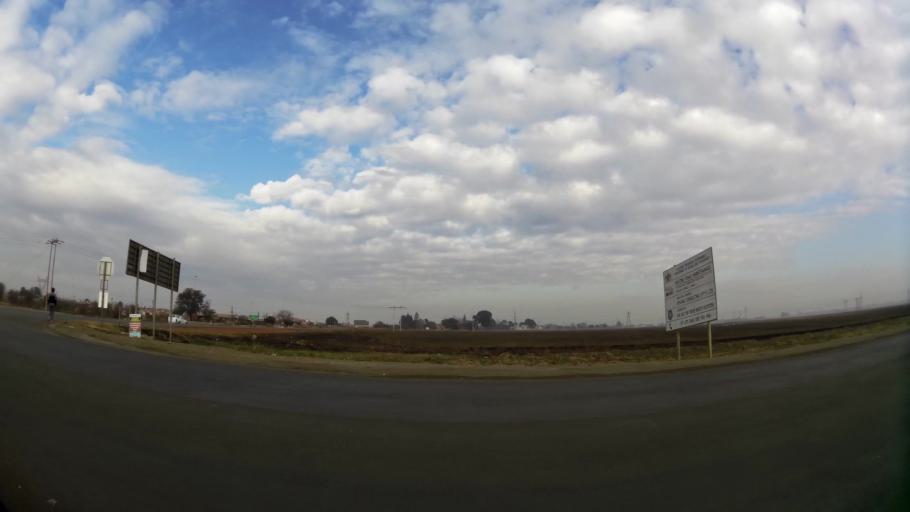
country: ZA
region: Gauteng
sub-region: Sedibeng District Municipality
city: Vanderbijlpark
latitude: -26.6731
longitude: 27.7907
